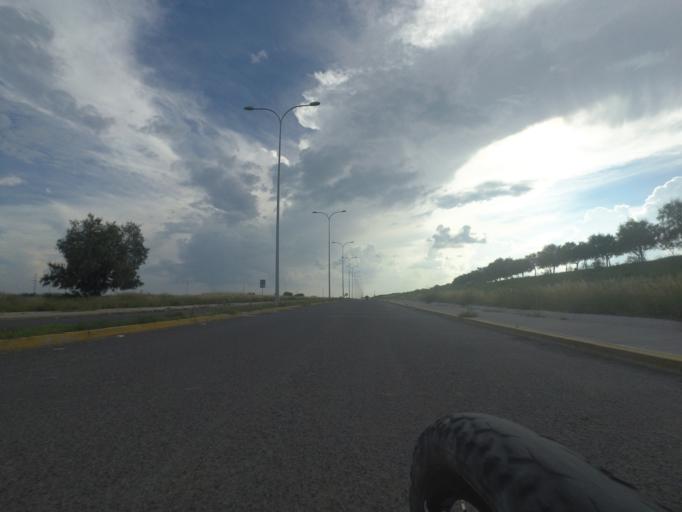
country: MX
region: Aguascalientes
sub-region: Aguascalientes
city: Penuelas (El Cienegal)
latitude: 21.7301
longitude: -102.2832
